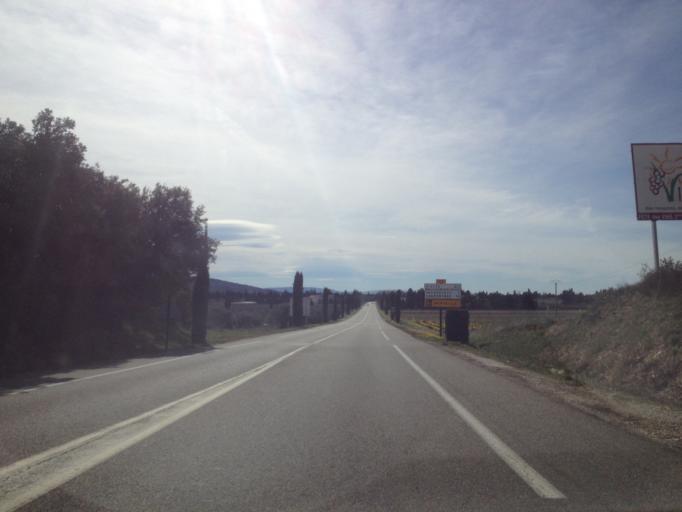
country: FR
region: Provence-Alpes-Cote d'Azur
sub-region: Departement du Vaucluse
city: Violes
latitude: 44.1833
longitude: 4.9543
